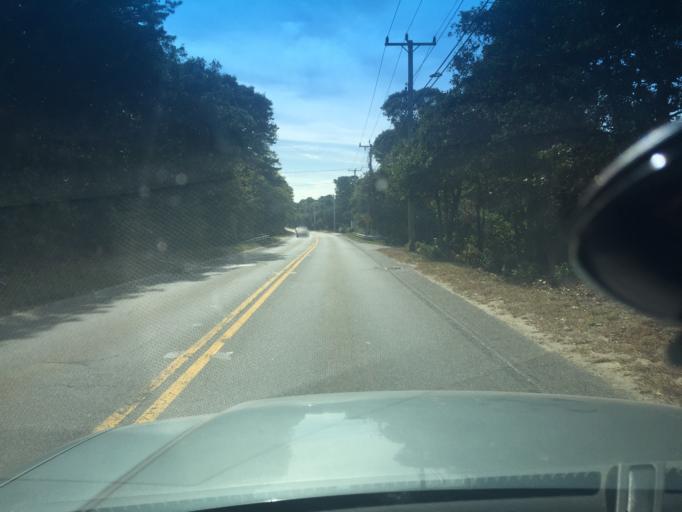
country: US
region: Massachusetts
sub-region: Barnstable County
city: Pocasset
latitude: 41.6722
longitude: -70.6000
